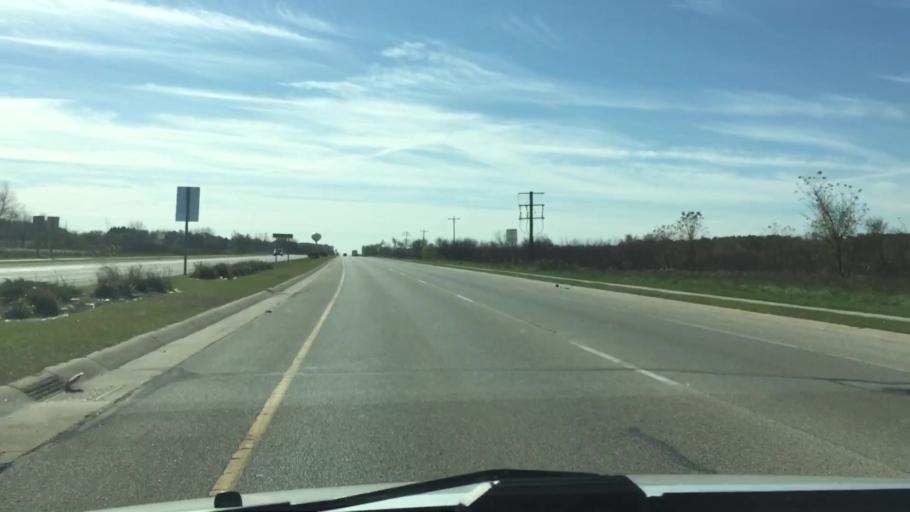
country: US
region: Wisconsin
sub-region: Waukesha County
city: Sussex
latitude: 43.1337
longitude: -88.2441
